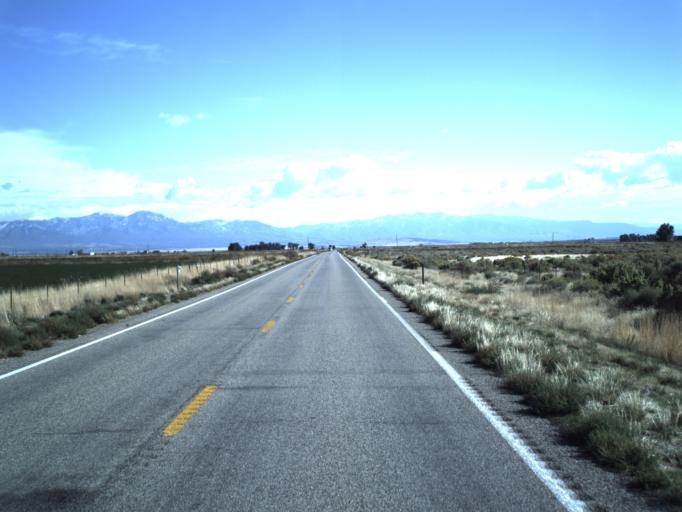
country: US
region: Utah
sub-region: Millard County
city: Delta
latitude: 39.2186
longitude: -112.4194
